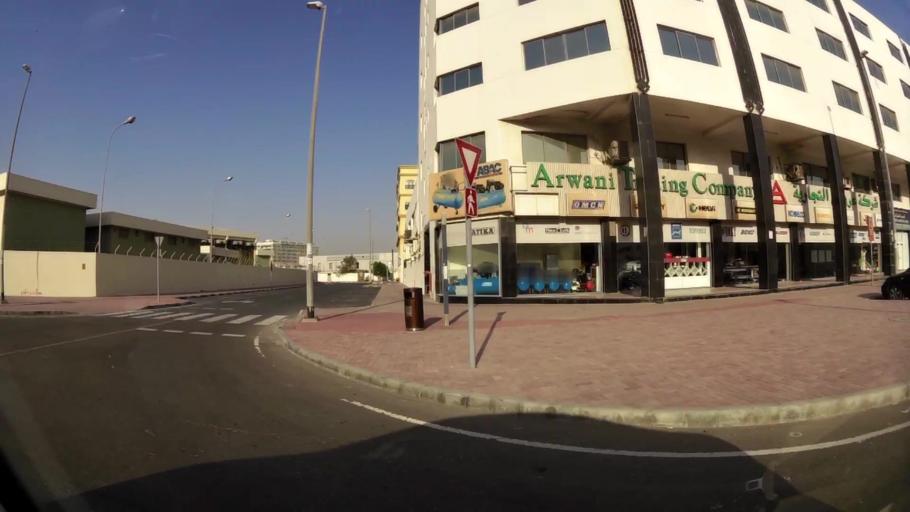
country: AE
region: Ash Shariqah
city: Sharjah
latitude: 25.2533
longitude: 55.3380
